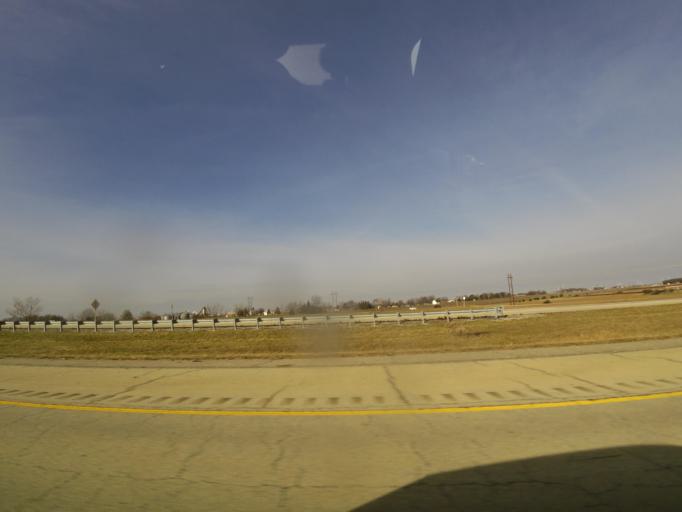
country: US
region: Illinois
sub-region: Macon County
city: Forsyth
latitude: 39.8956
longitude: -89.0056
